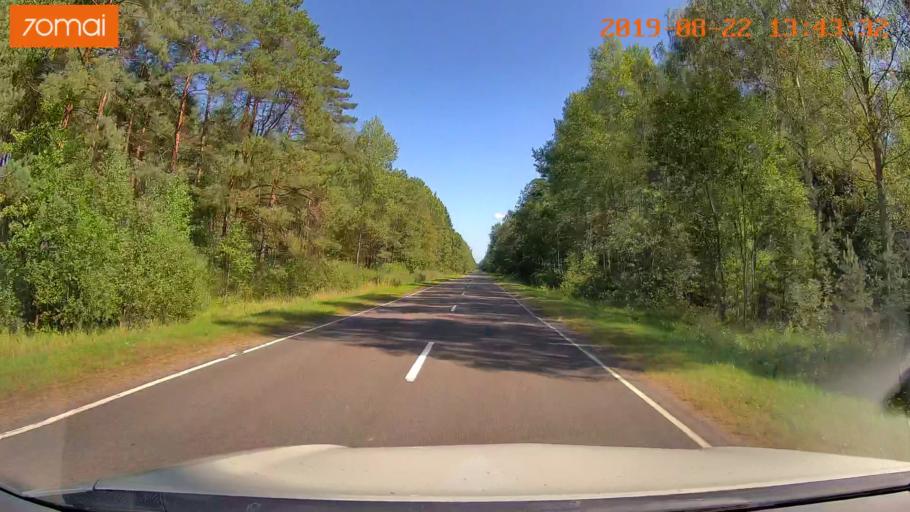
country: BY
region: Mogilev
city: Asipovichy
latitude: 53.2429
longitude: 28.4398
